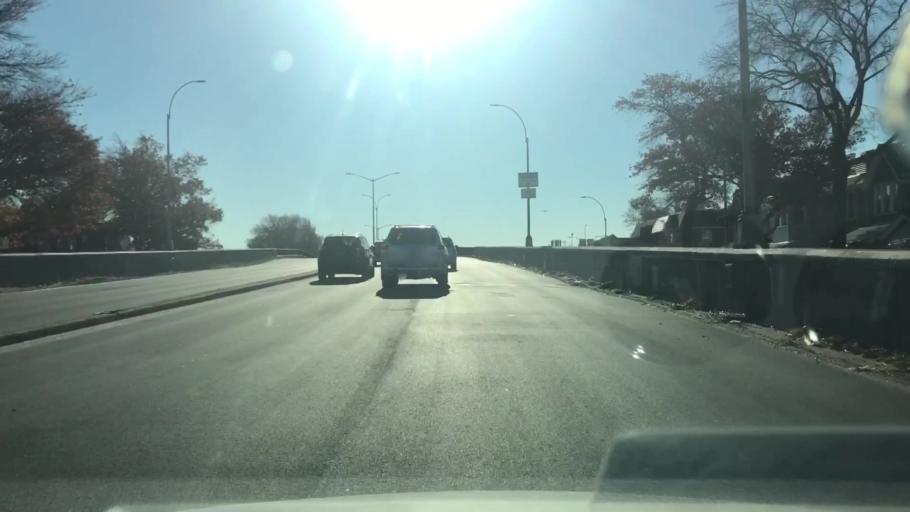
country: US
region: New York
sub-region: Queens County
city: Borough of Queens
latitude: 40.6891
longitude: -73.8497
